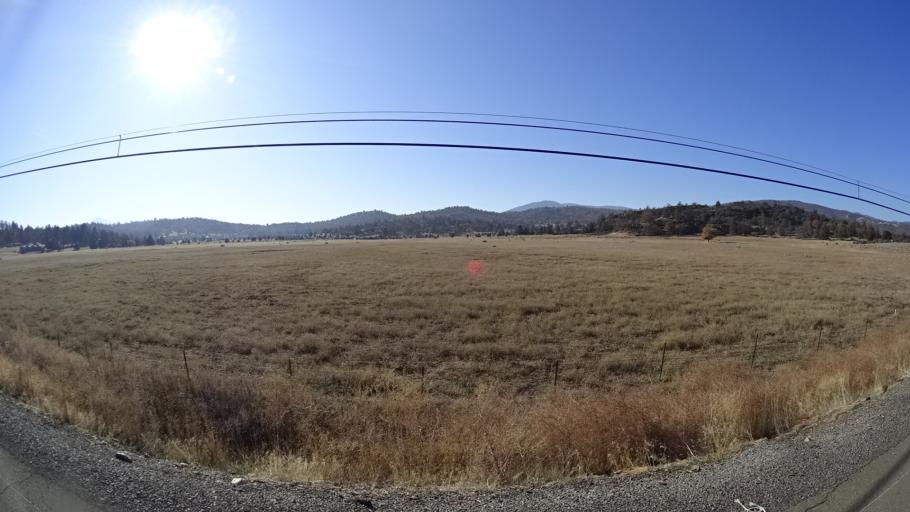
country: US
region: California
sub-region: Siskiyou County
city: Yreka
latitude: 41.7110
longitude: -122.5866
